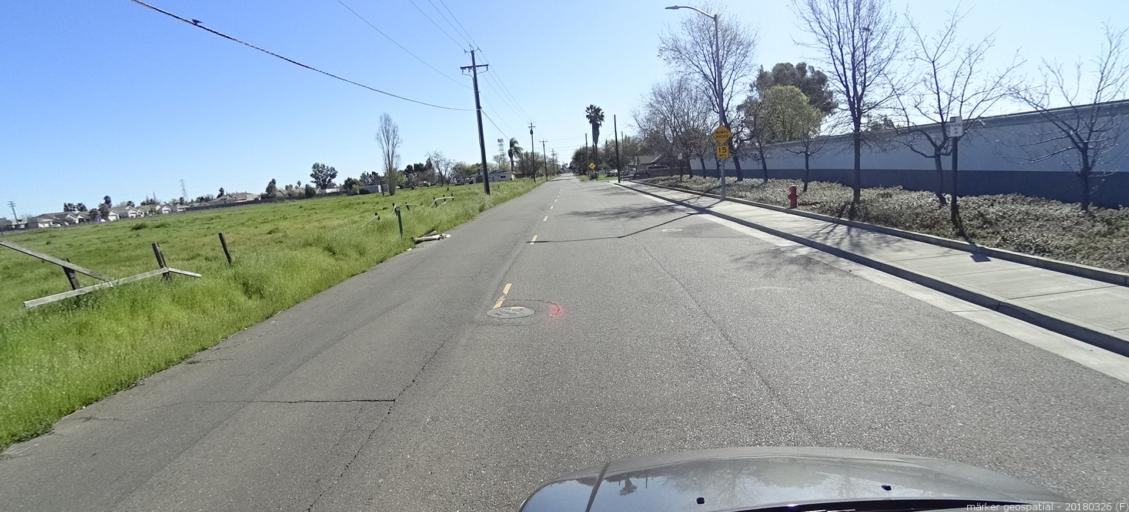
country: US
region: California
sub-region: Sacramento County
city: Florin
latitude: 38.4652
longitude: -121.4129
